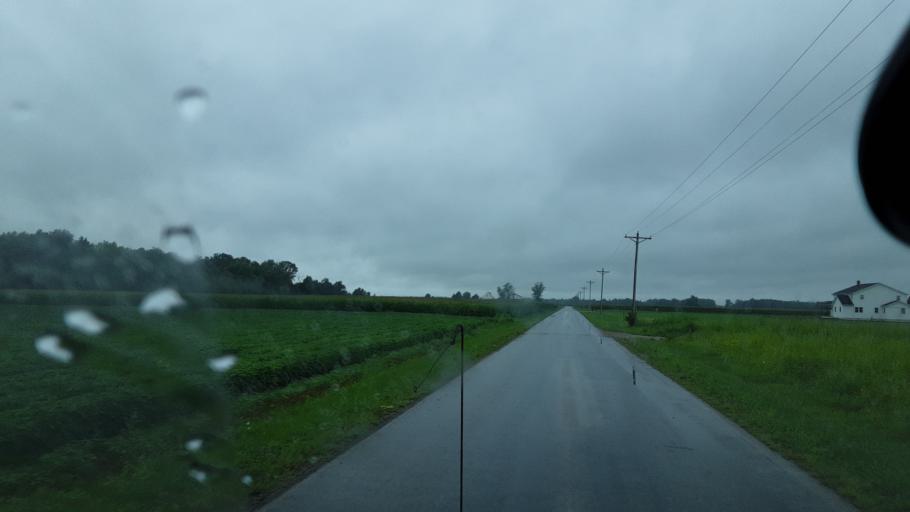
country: US
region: Indiana
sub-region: Adams County
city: Decatur
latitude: 40.7528
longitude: -84.8568
